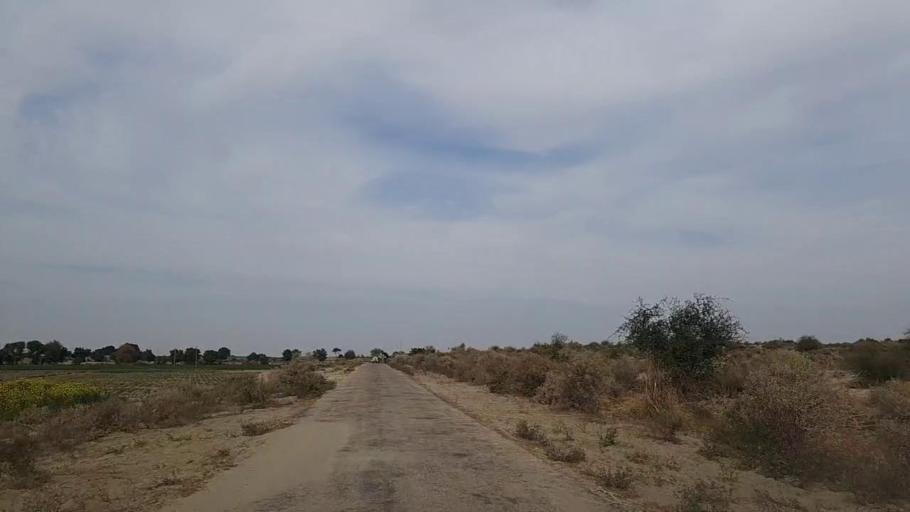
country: PK
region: Sindh
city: Jam Sahib
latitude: 26.4427
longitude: 68.6114
